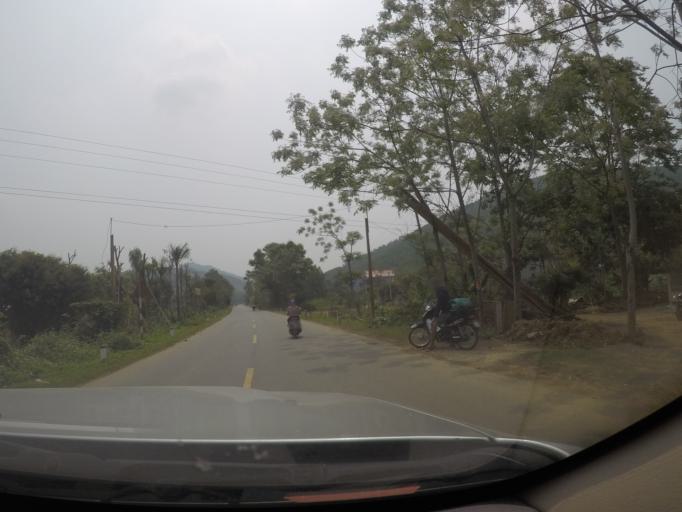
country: VN
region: Thanh Hoa
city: Thi Tran Cam Thuy
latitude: 20.1836
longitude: 105.4767
